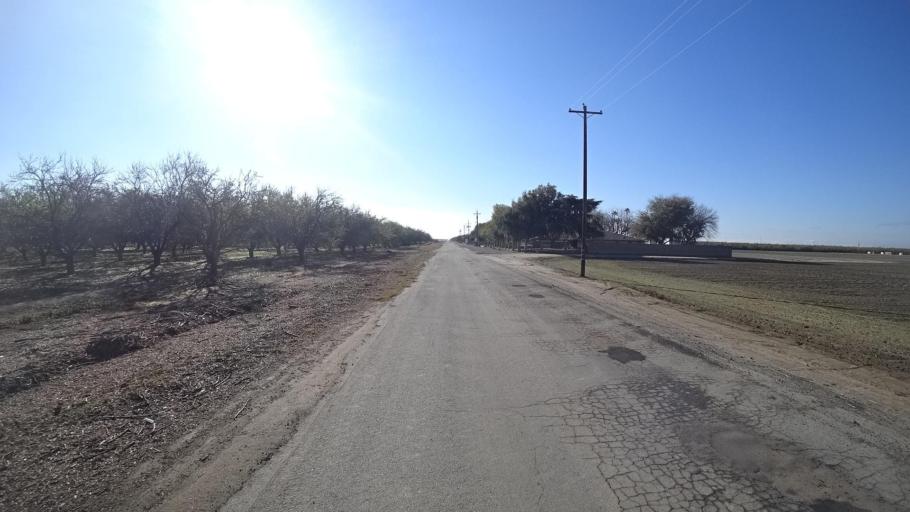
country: US
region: California
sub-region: Kern County
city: McFarland
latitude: 35.6840
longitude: -119.2675
